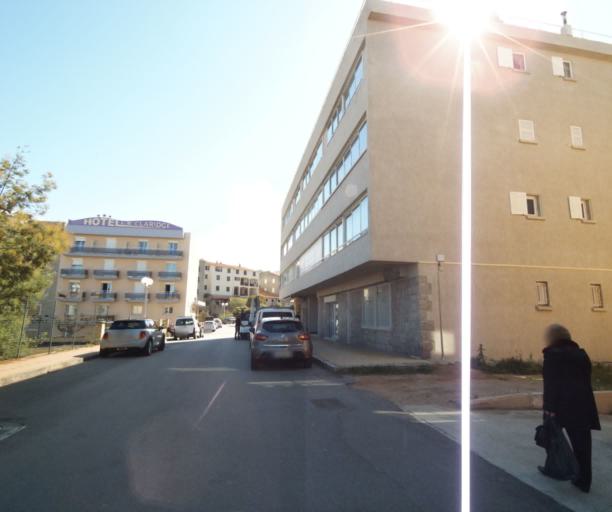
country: FR
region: Corsica
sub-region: Departement de la Corse-du-Sud
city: Propriano
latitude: 41.6745
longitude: 8.9031
